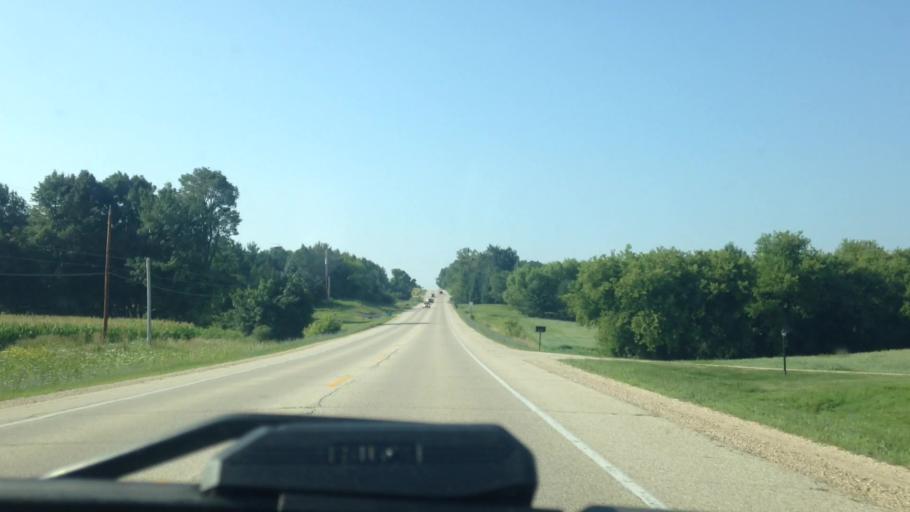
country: US
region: Wisconsin
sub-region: Washington County
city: Richfield
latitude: 43.2416
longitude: -88.2618
